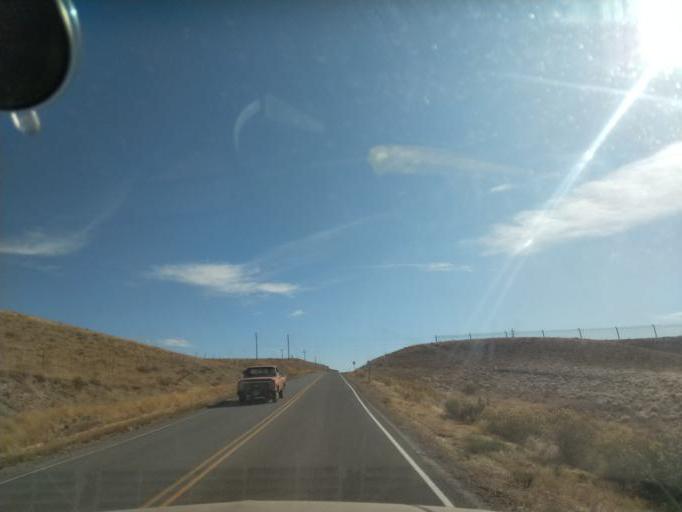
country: US
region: Colorado
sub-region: Mesa County
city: Fruitvale
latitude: 39.0165
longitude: -108.4845
